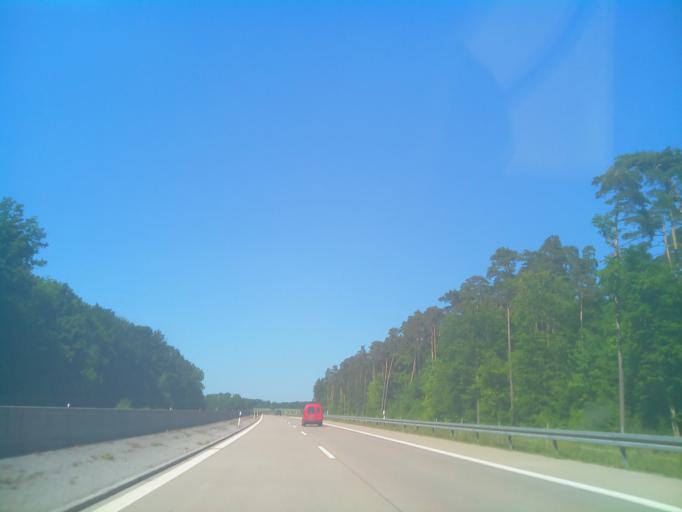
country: DE
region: Bavaria
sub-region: Regierungsbezirk Unterfranken
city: Strahlungen
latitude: 50.2816
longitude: 10.2599
